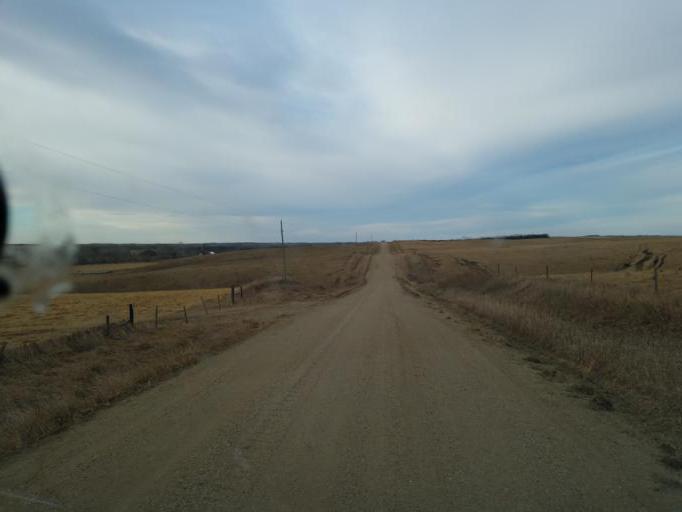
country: US
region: Nebraska
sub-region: Knox County
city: Bloomfield
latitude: 42.5577
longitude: -97.7340
